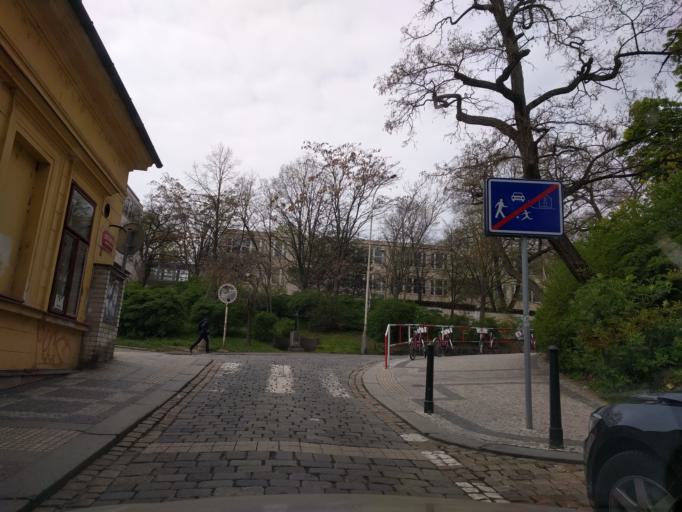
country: CZ
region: Praha
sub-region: Praha 1
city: Mala Strana
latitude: 50.1039
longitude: 14.4083
